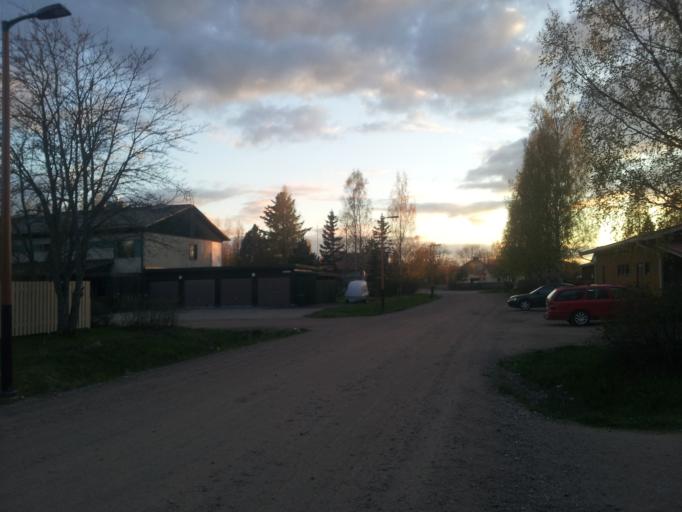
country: FI
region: Haeme
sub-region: Riihimaeki
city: Riihimaeki
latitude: 60.7524
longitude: 24.7793
